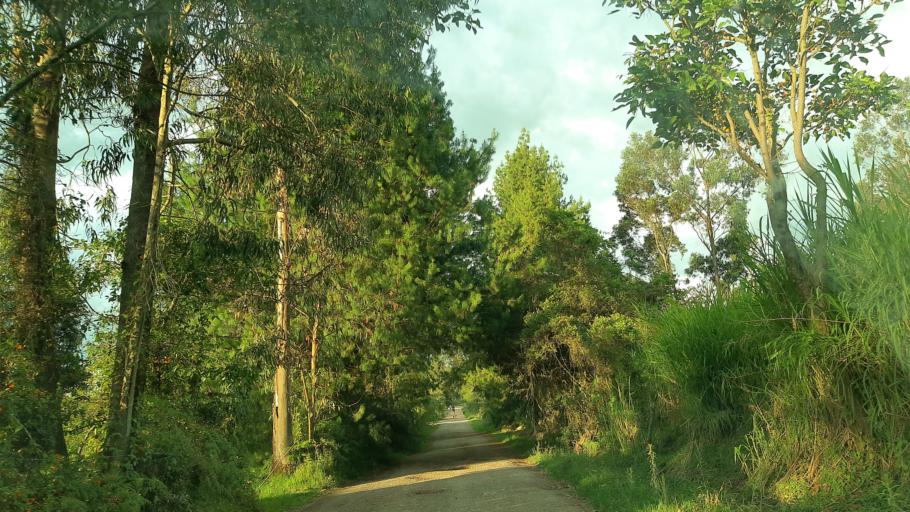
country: CO
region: Boyaca
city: La Capilla
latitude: 5.7100
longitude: -73.4807
